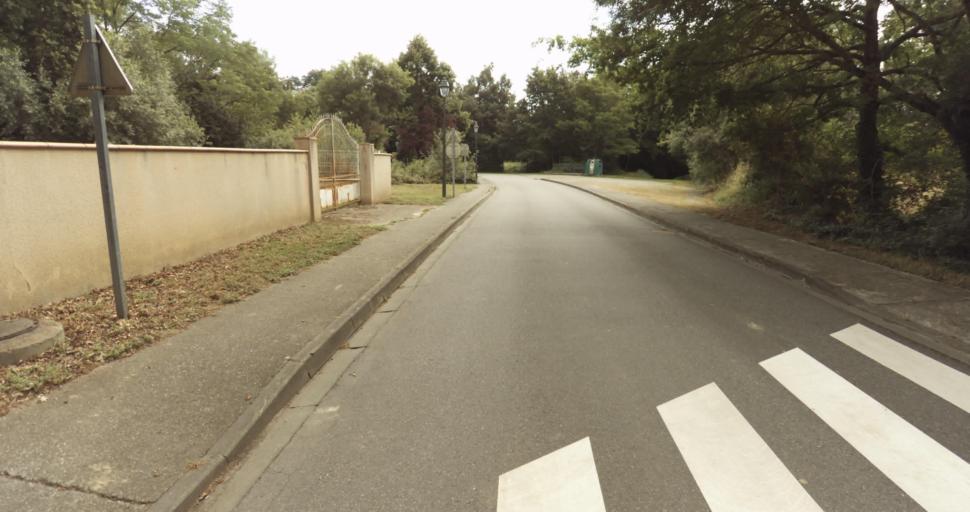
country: FR
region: Midi-Pyrenees
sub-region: Departement de la Haute-Garonne
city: Fontenilles
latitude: 43.5527
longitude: 1.1944
